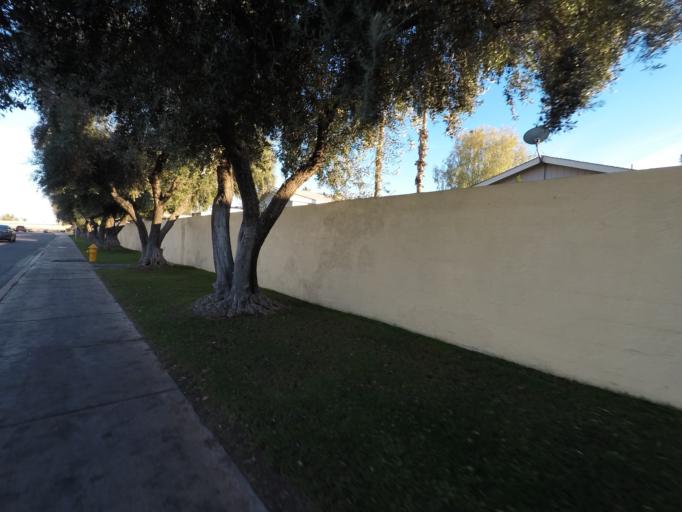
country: US
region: Arizona
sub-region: Maricopa County
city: Guadalupe
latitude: 33.3927
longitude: -111.9714
